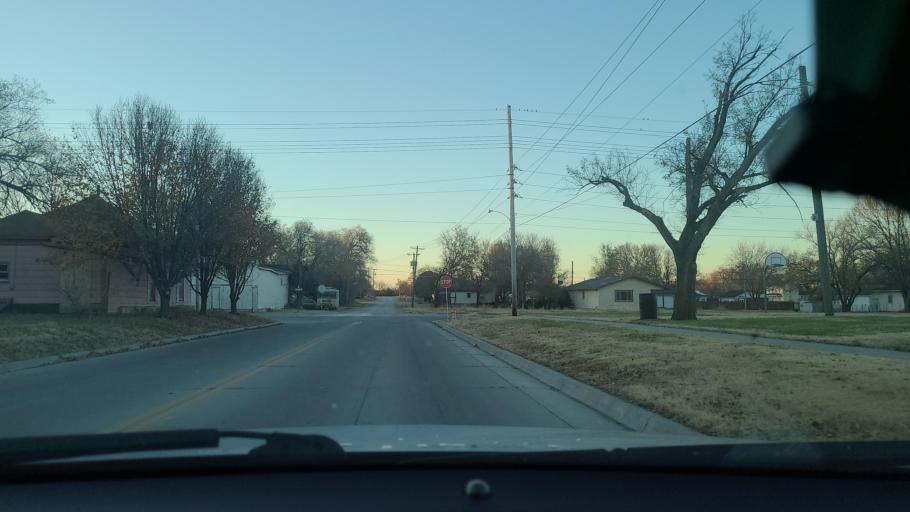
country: US
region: Kansas
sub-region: Sumner County
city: Wellington
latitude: 37.2655
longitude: -97.3852
